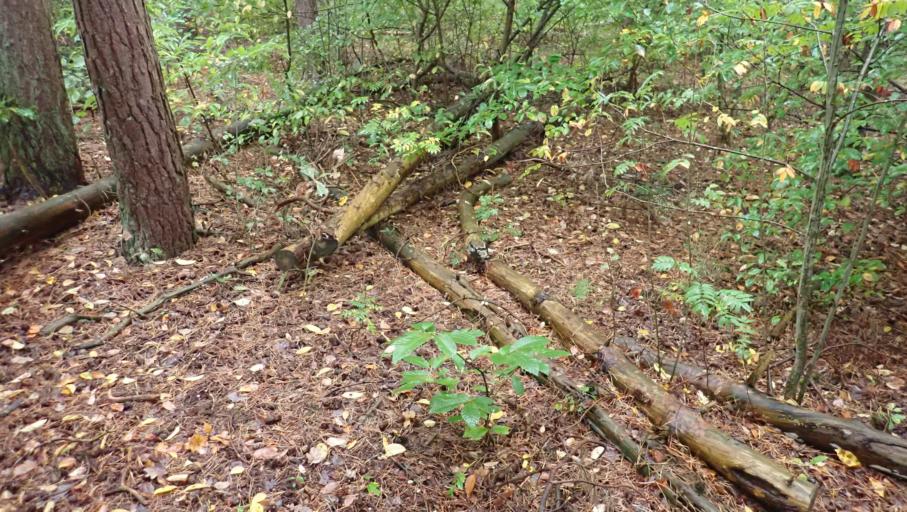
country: BE
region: Flanders
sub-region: Provincie Antwerpen
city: Nijlen
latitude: 51.1486
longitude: 4.6800
